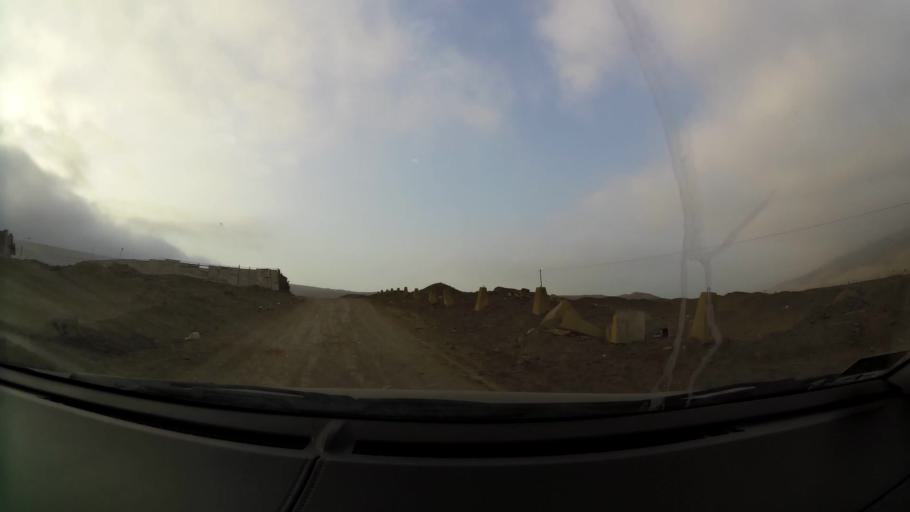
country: PE
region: Lima
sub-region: Lima
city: Santa Rosa
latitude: -11.7336
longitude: -77.1367
